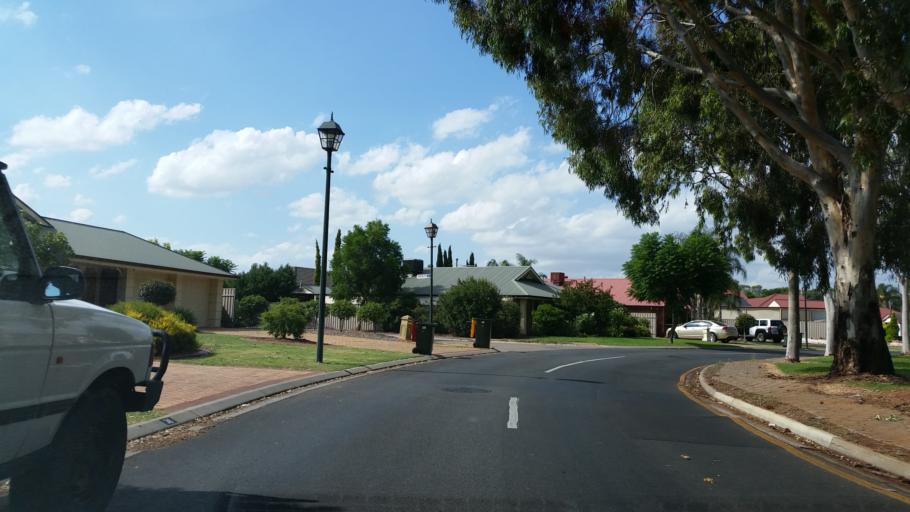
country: AU
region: South Australia
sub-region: Salisbury
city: Salisbury
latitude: -34.7818
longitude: 138.6258
